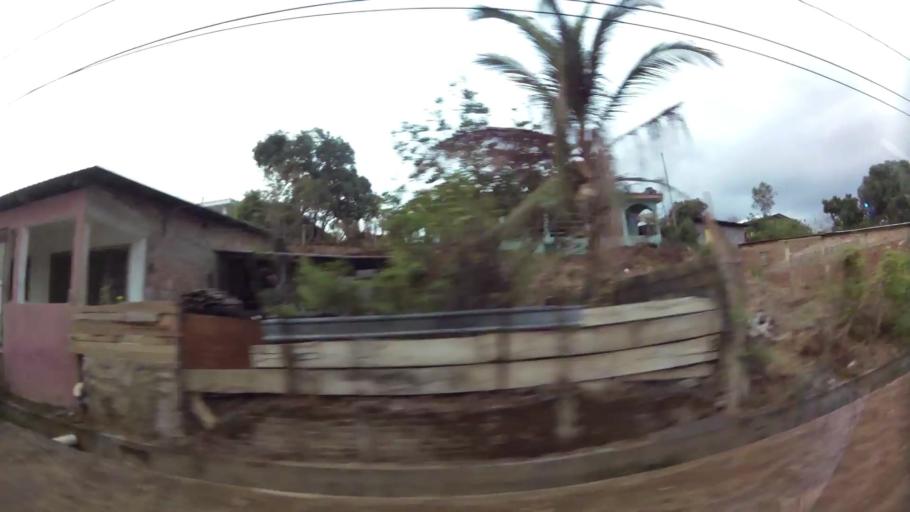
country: NI
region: Rivas
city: San Juan del Sur
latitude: 11.2636
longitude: -85.8772
